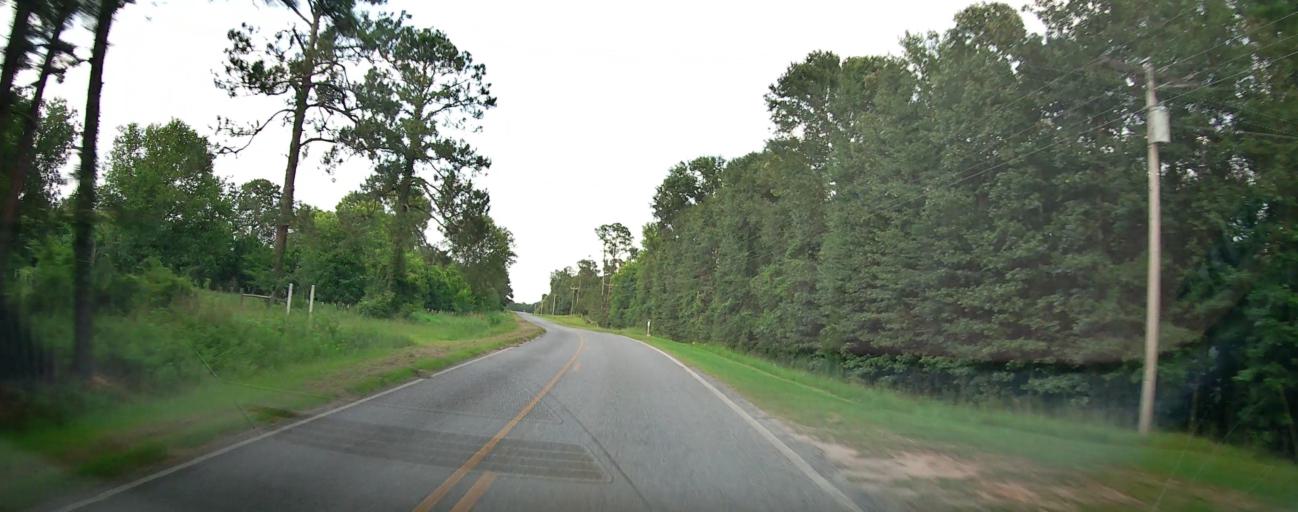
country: US
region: Georgia
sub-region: Crawford County
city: Roberta
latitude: 32.6527
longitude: -84.0278
